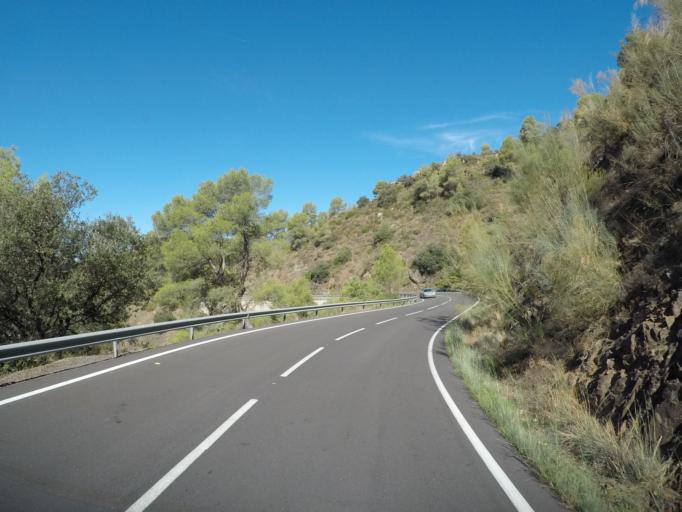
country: ES
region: Catalonia
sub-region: Provincia de Tarragona
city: Falset
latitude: 41.1730
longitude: 0.7983
